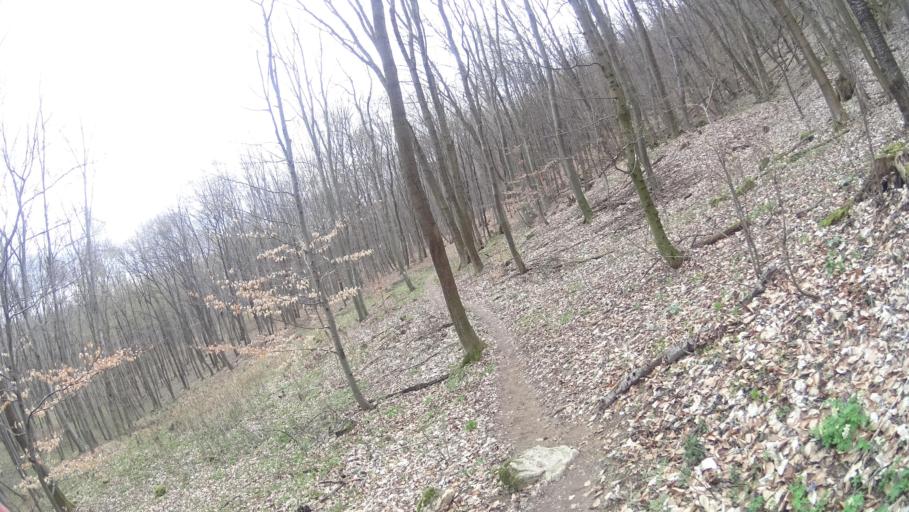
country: HU
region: Pest
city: Kosd
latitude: 47.8398
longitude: 19.1436
